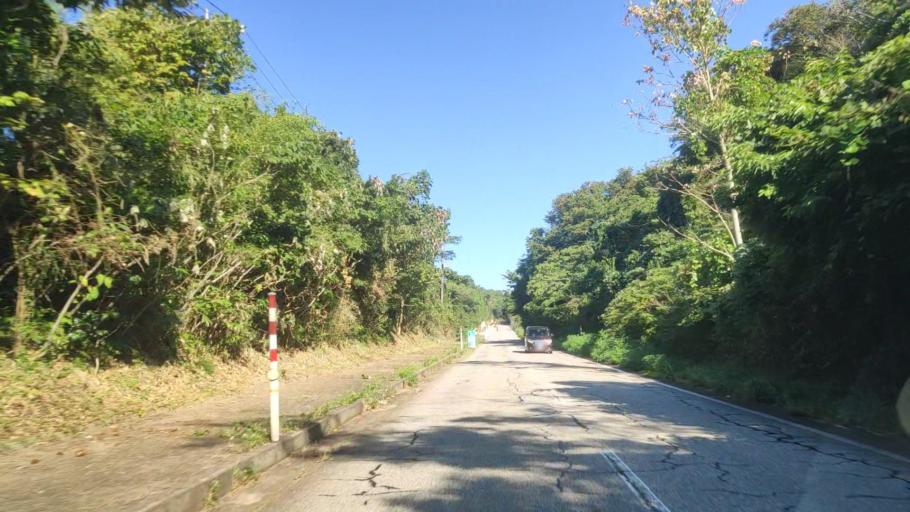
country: JP
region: Ishikawa
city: Hakui
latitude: 37.0855
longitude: 136.7300
